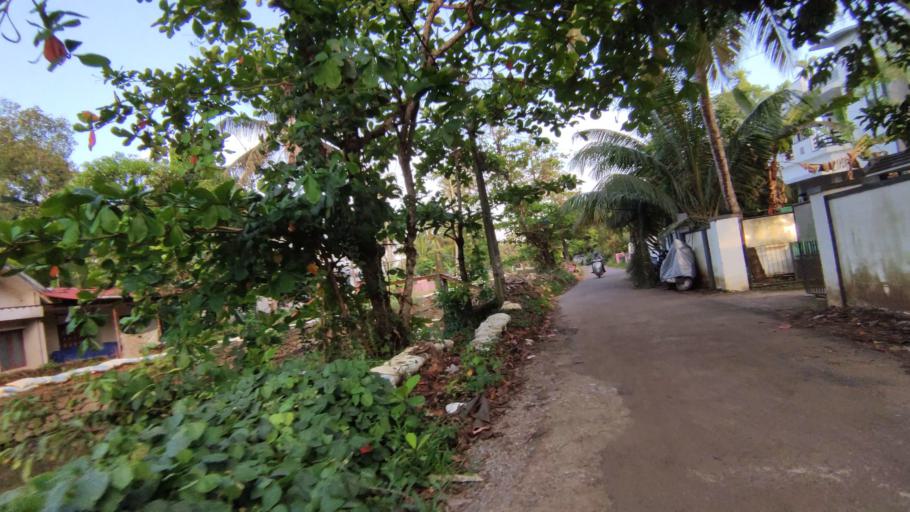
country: IN
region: Kerala
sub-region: Kottayam
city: Kottayam
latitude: 9.5956
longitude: 76.4610
